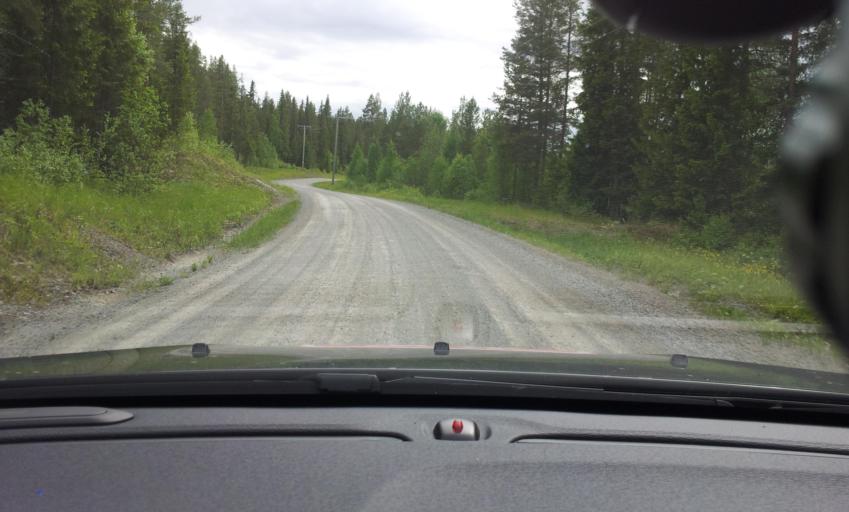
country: SE
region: Jaemtland
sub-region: OEstersunds Kommun
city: Brunflo
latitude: 62.9954
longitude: 14.7339
